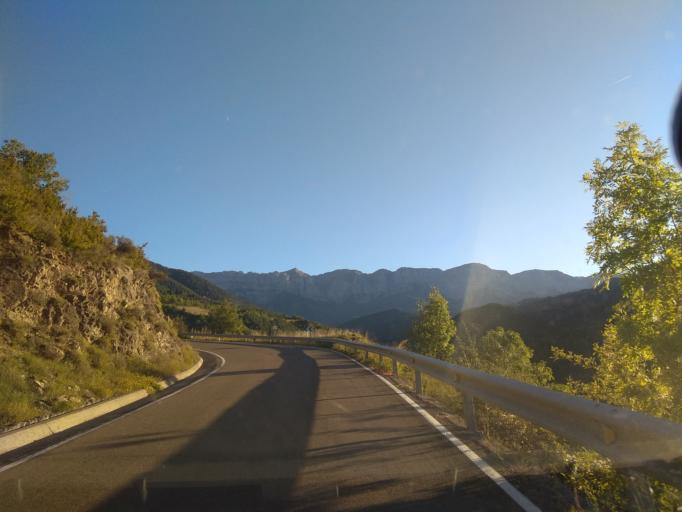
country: ES
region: Catalonia
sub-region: Provincia de Lleida
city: Lles de Cerdanya
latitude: 42.3511
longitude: 1.6893
